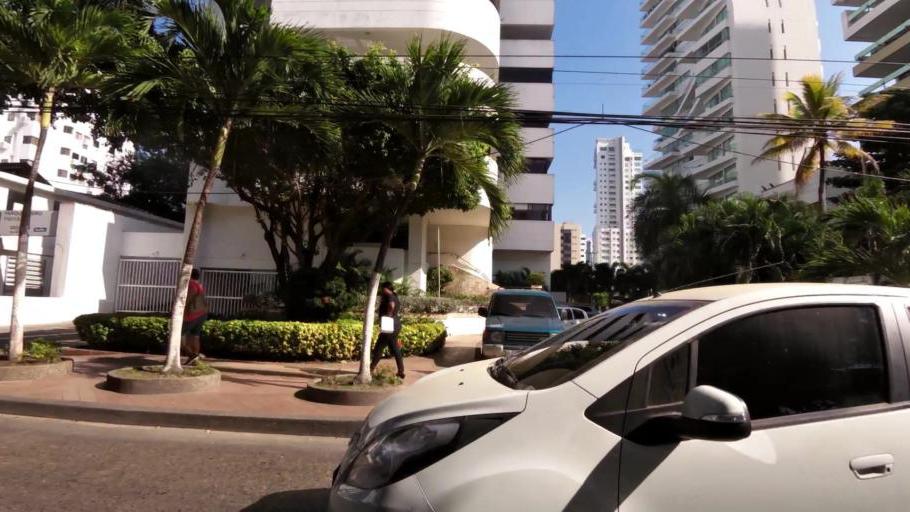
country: CO
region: Bolivar
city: Cartagena
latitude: 10.4016
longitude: -75.5553
